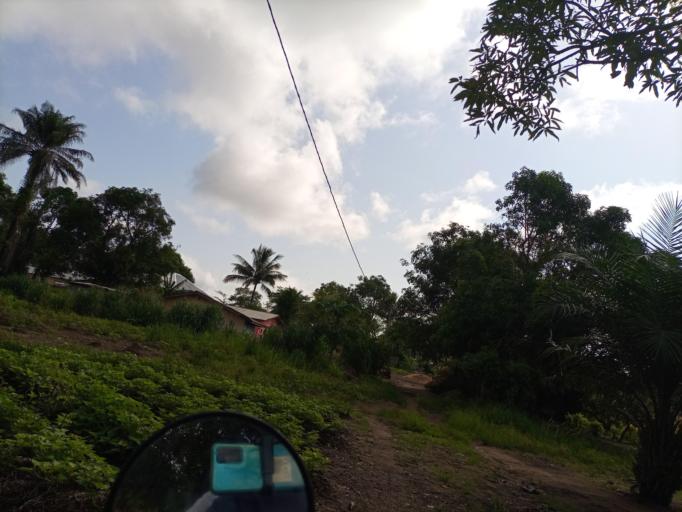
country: SL
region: Southern Province
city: Bo
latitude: 7.9641
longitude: -11.7644
